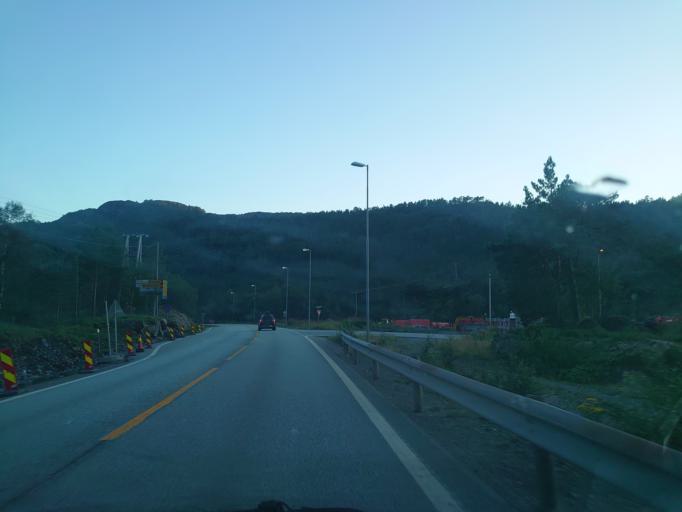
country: NO
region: Hordaland
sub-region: Osteroy
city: Lonevag
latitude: 60.6650
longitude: 5.4871
